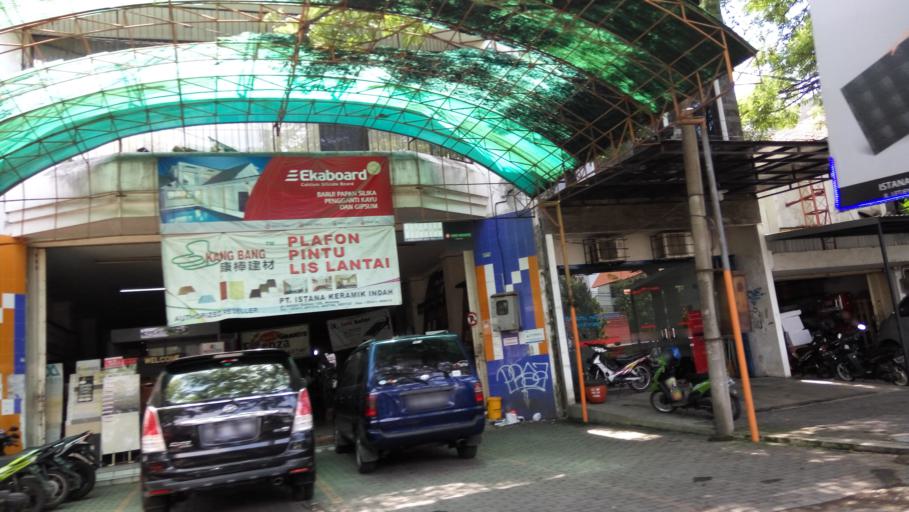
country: ID
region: East Java
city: Malang
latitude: -7.9573
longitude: 112.6380
